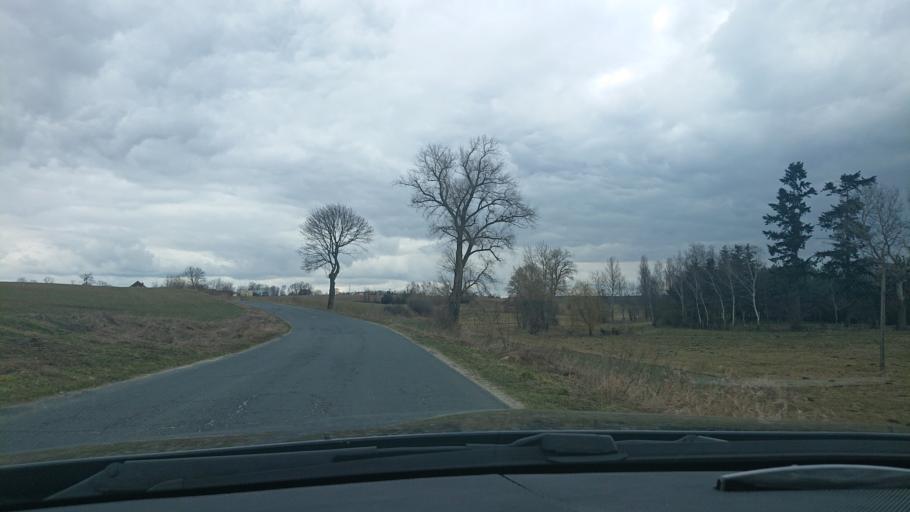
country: PL
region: Greater Poland Voivodeship
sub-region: Powiat gnieznienski
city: Gniezno
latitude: 52.5815
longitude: 17.6592
